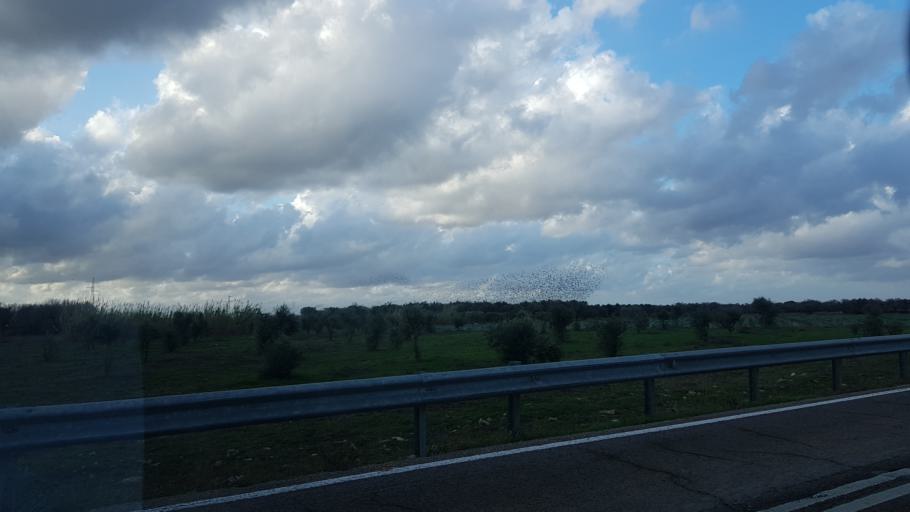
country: IT
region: Apulia
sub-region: Provincia di Brindisi
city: San Pietro Vernotico
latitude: 40.5200
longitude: 18.0148
